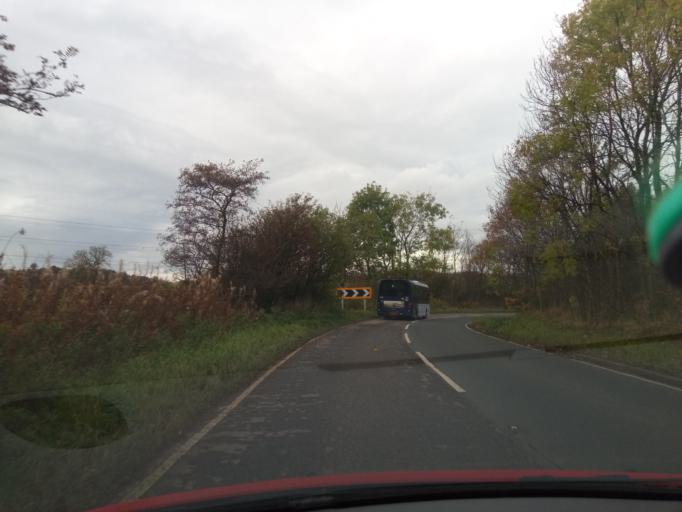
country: GB
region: Scotland
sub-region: West Lothian
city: Blackburn
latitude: 55.8473
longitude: -3.6110
